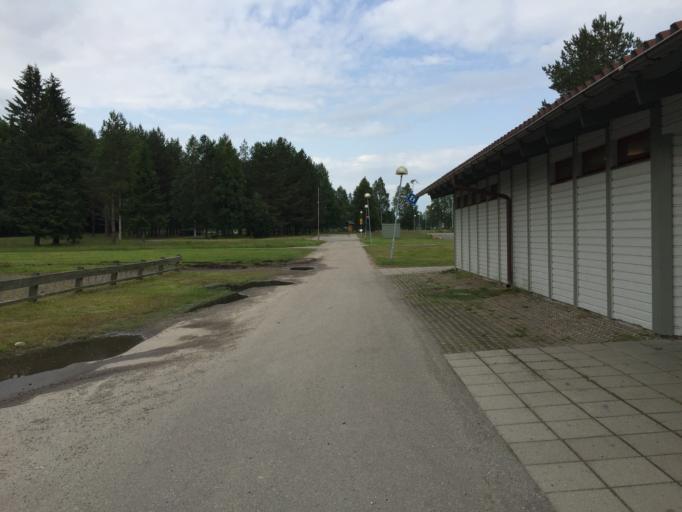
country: SE
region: Vaesterbotten
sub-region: Umea Kommun
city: Ersmark
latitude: 63.8375
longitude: 20.3396
